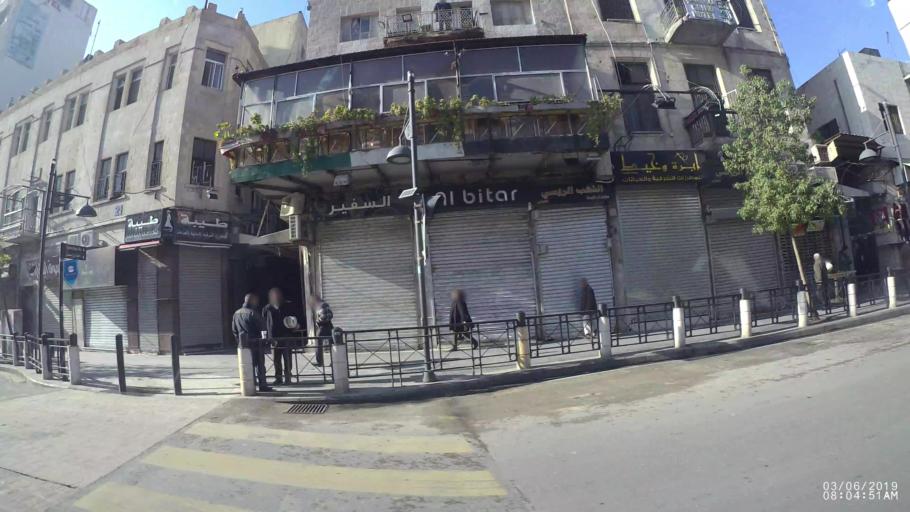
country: JO
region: Amman
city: Amman
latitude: 31.9518
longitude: 35.9329
